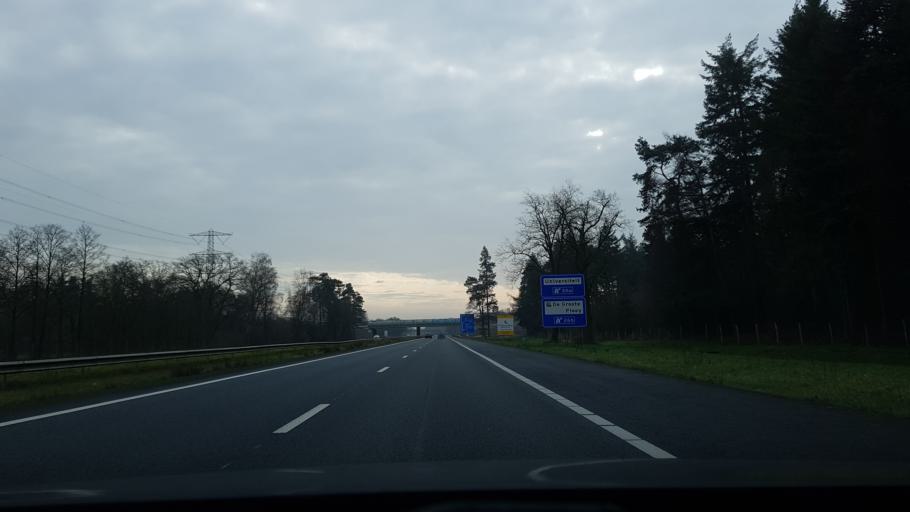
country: NL
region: Overijssel
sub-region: Gemeente Hengelo
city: Hengelo
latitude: 52.2210
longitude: 6.7961
